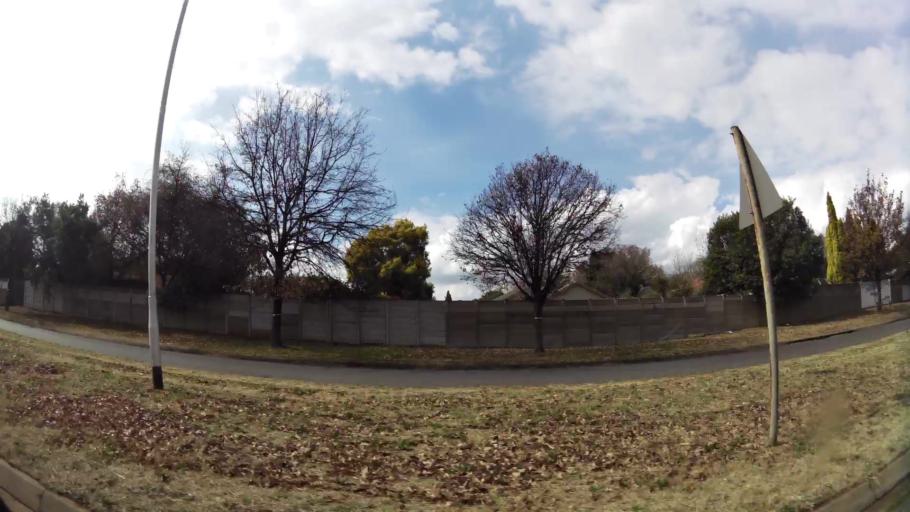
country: ZA
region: Gauteng
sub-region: Sedibeng District Municipality
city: Vanderbijlpark
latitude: -26.7375
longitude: 27.8436
